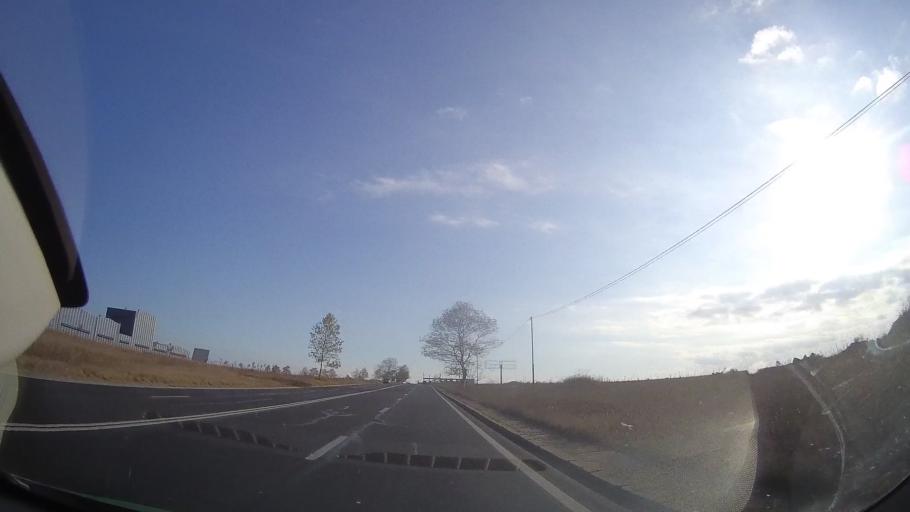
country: RO
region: Constanta
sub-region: Municipiul Mangalia
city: Mangalia
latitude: 43.7973
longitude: 28.5595
